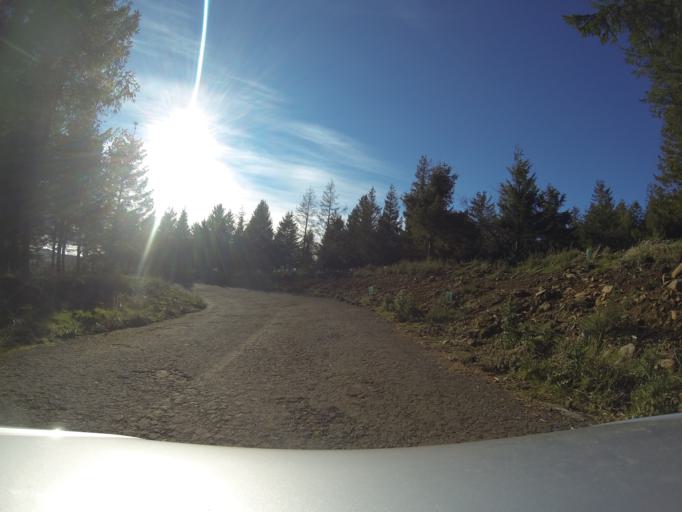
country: PT
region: Madeira
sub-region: Sao Vicente
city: Sao Vicente
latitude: 32.7712
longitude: -17.0775
